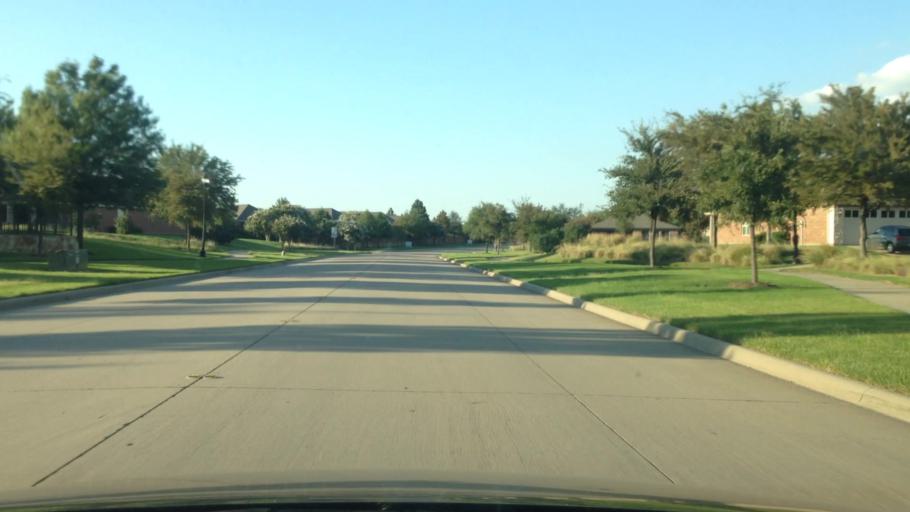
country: US
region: Texas
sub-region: Denton County
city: Little Elm
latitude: 33.1423
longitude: -96.8968
